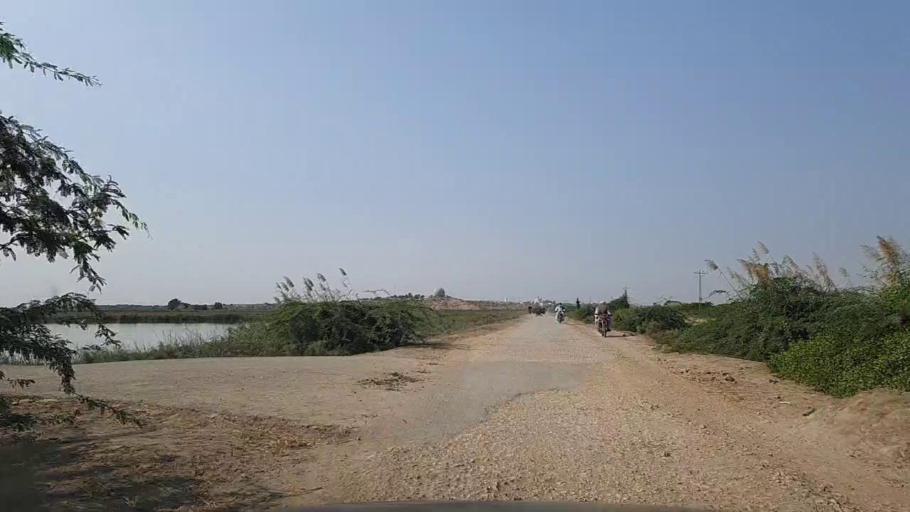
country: PK
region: Sindh
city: Chuhar Jamali
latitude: 24.5481
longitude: 67.8986
